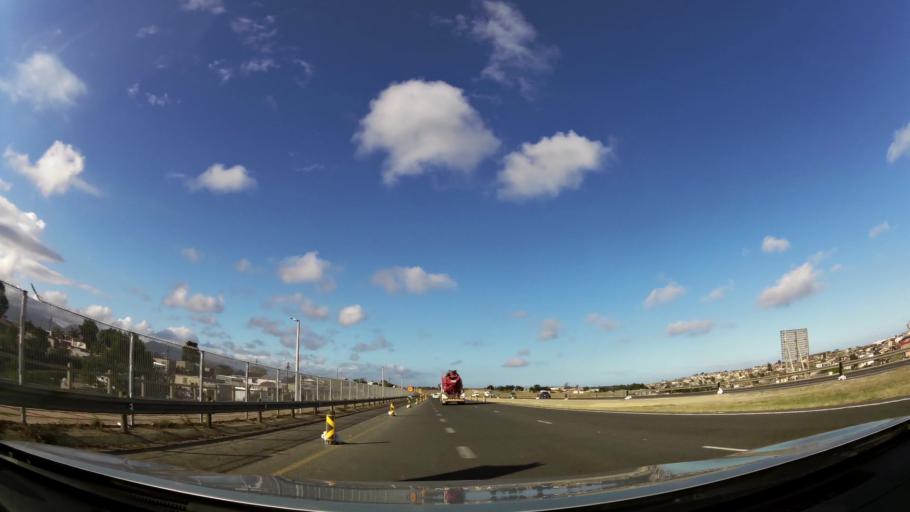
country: ZA
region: Western Cape
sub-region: Eden District Municipality
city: George
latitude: -33.9955
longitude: 22.4809
